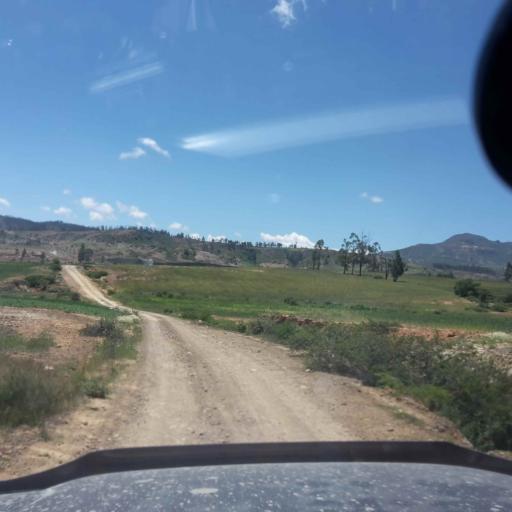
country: BO
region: Cochabamba
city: Totora
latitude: -17.7753
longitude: -65.2539
